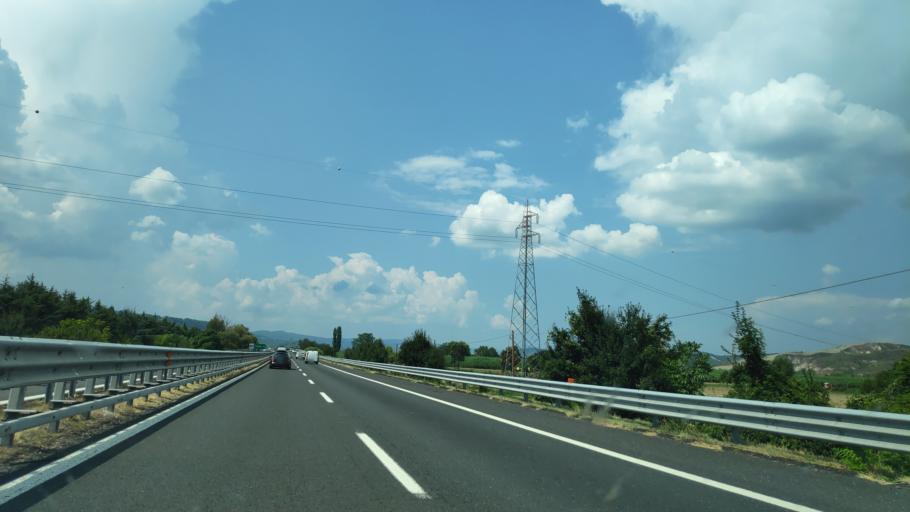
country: IT
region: Umbria
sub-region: Provincia di Terni
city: Sferracavallo
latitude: 42.7345
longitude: 12.1071
